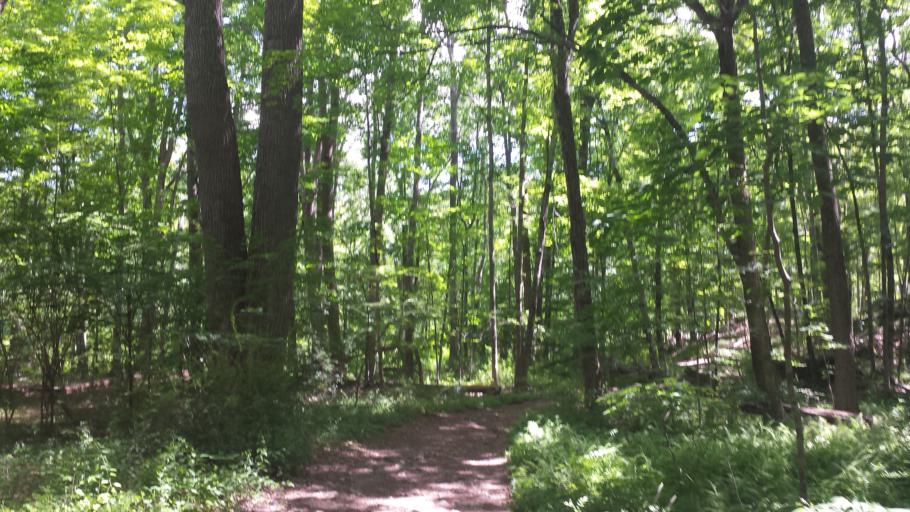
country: US
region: New York
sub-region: Westchester County
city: Pound Ridge
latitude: 41.2614
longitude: -73.5783
